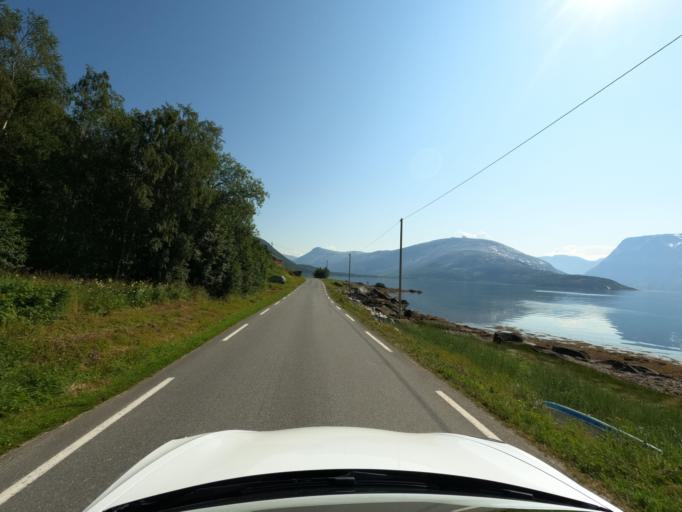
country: NO
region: Nordland
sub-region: Narvik
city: Narvik
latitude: 68.2816
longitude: 17.3807
